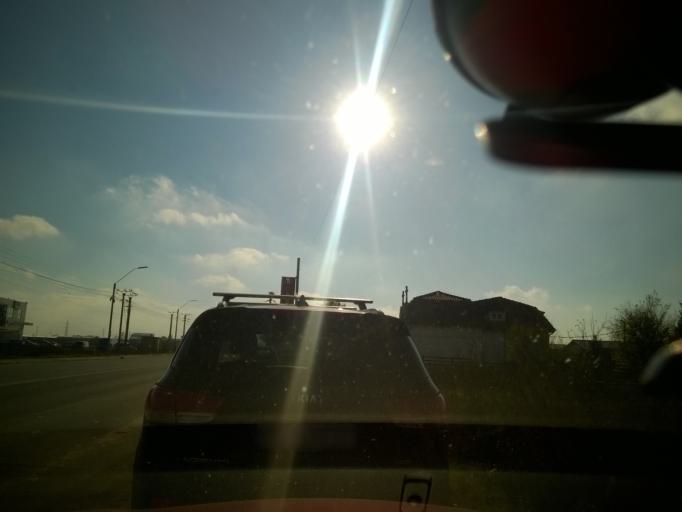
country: RO
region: Ilfov
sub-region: Comuna Magurele
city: Magurele
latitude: 44.3720
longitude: 26.0440
